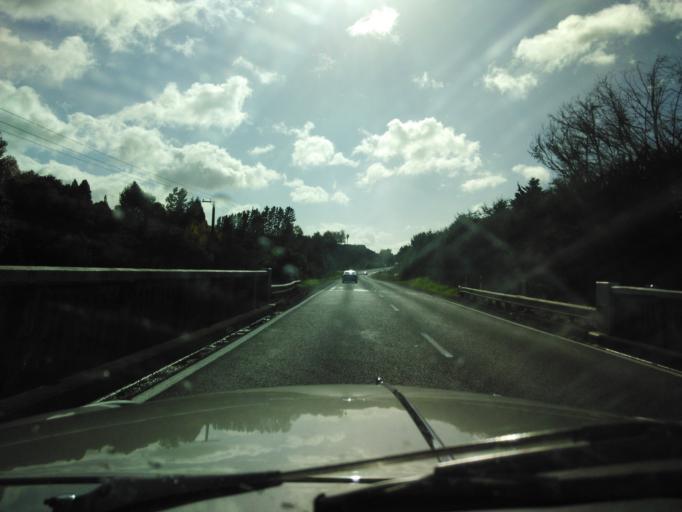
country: NZ
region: Bay of Plenty
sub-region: Western Bay of Plenty District
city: Katikati
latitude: -37.4948
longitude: 175.9273
